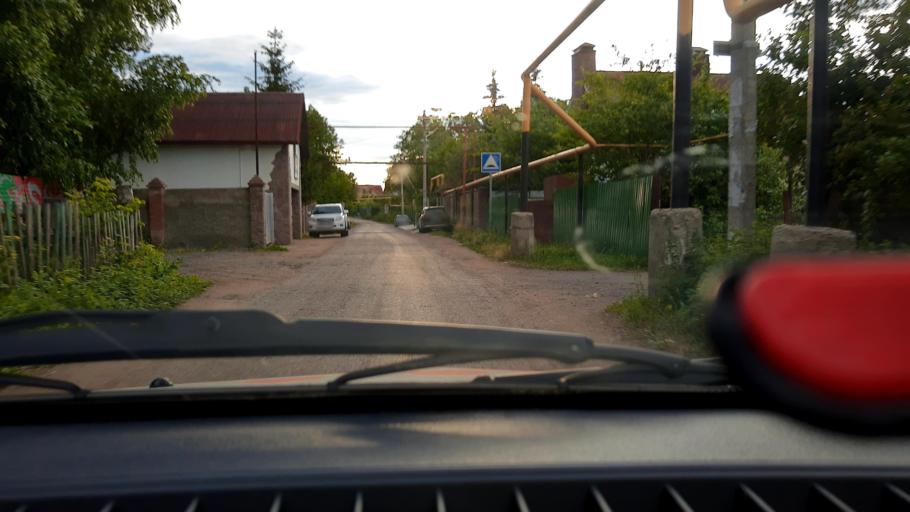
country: RU
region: Bashkortostan
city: Ufa
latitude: 54.6740
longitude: 55.8538
